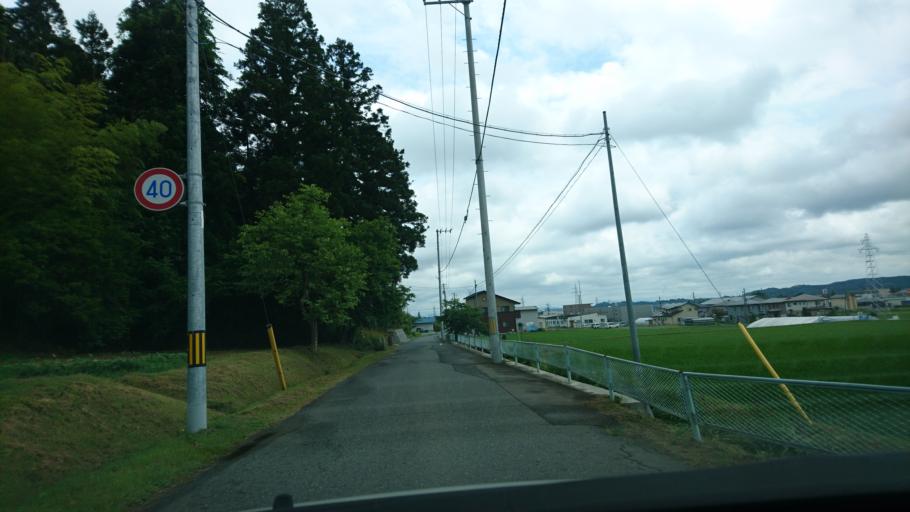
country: JP
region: Iwate
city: Ichinoseki
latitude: 38.9432
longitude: 141.0899
